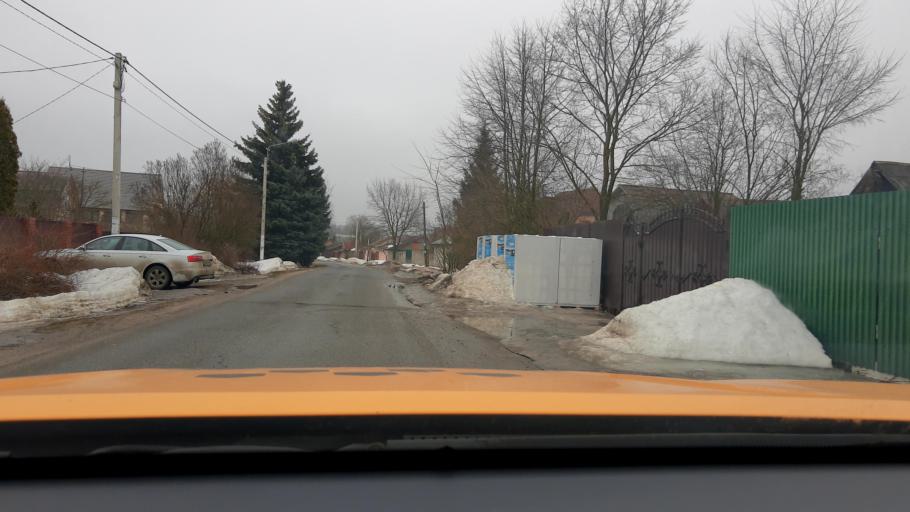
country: RU
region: Moskovskaya
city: Yamkino
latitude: 55.9172
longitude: 38.4442
